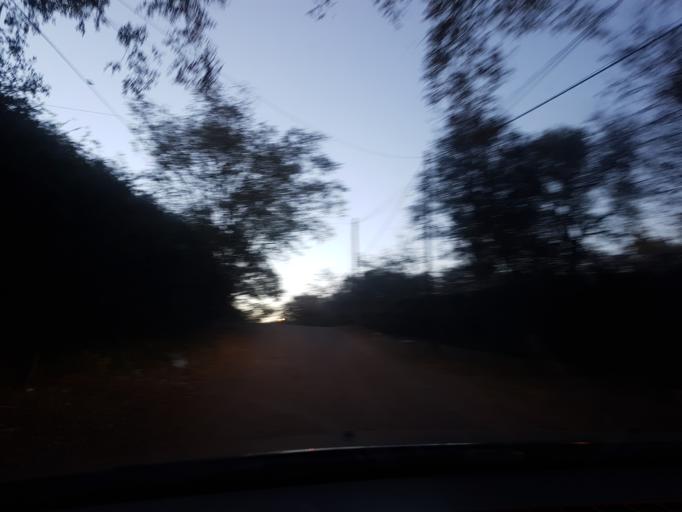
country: AR
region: Cordoba
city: Villa Allende
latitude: -31.2784
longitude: -64.2834
